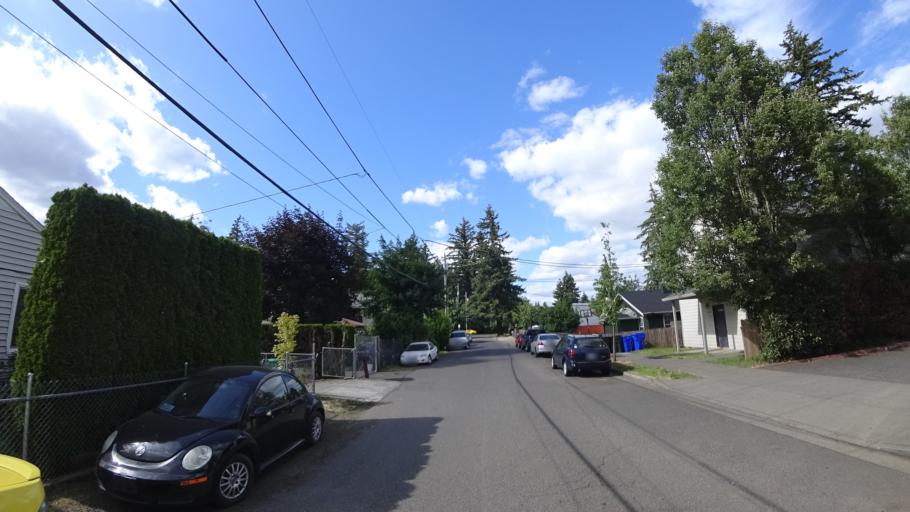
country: US
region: Oregon
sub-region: Multnomah County
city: Lents
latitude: 45.4960
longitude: -122.5405
